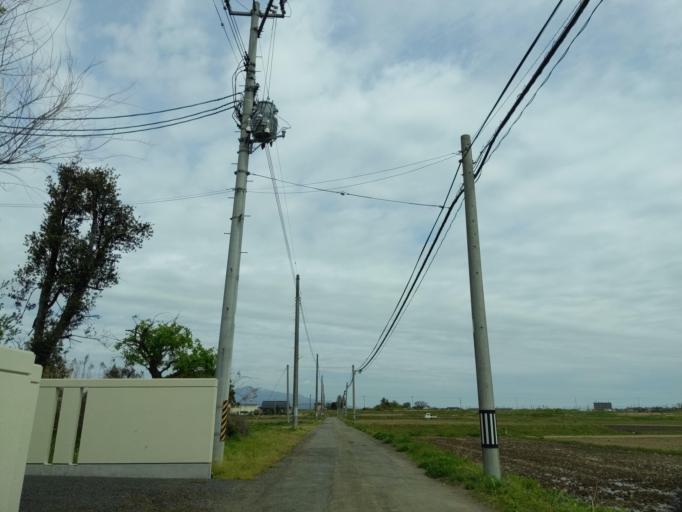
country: JP
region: Fukushima
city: Koriyama
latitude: 37.3773
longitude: 140.3237
